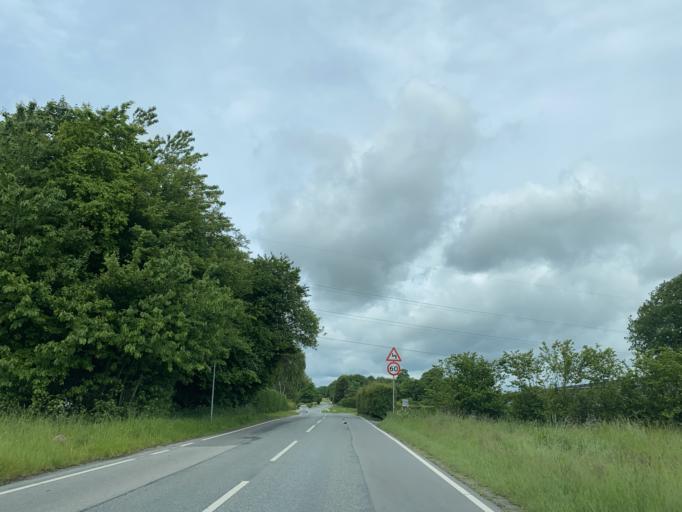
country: DK
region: Central Jutland
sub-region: Arhus Kommune
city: Trige
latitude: 56.1889
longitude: 10.1488
